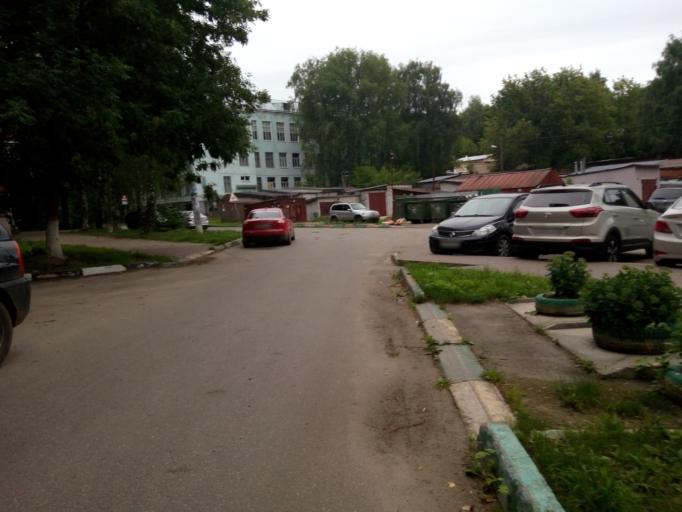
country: RU
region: Nizjnij Novgorod
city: Nizhniy Novgorod
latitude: 56.2734
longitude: 43.9807
